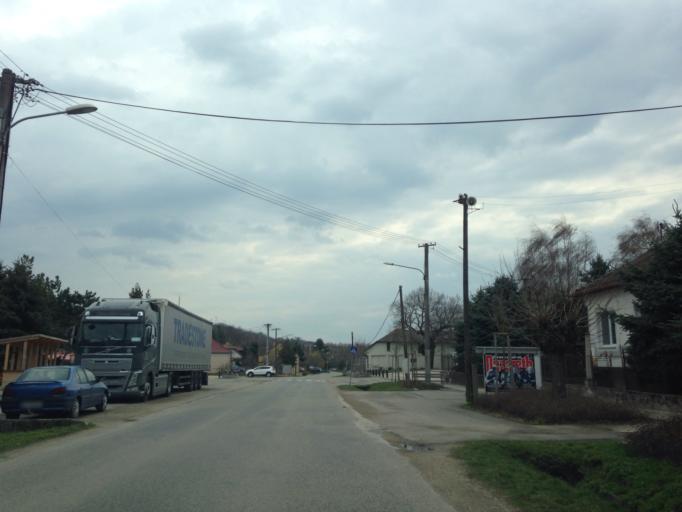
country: SK
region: Nitriansky
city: Svodin
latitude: 47.9581
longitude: 18.4118
